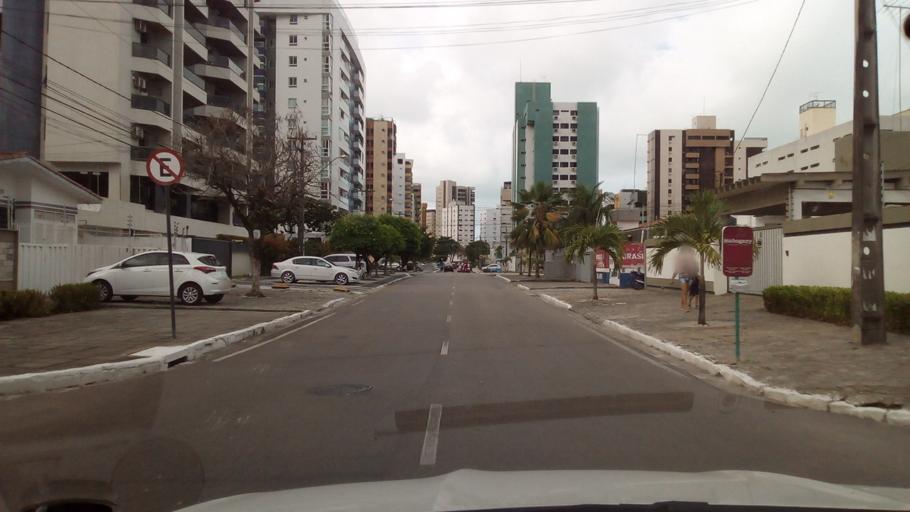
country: BR
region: Paraiba
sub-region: Joao Pessoa
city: Joao Pessoa
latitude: -7.1172
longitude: -34.8271
